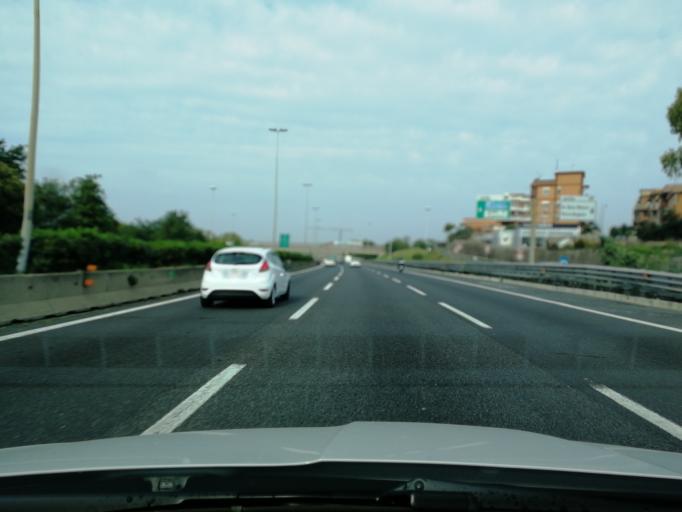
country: IT
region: Latium
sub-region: Citta metropolitana di Roma Capitale
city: Setteville
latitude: 41.8879
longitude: 12.6141
